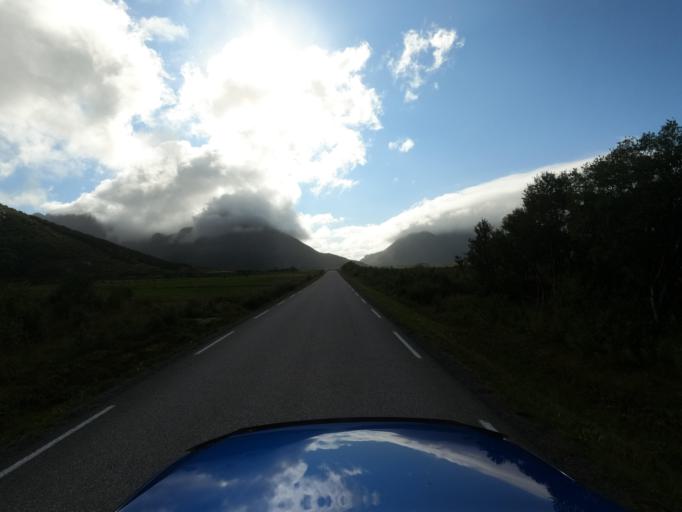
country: NO
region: Nordland
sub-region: Vagan
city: Kabelvag
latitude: 68.2992
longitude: 14.1679
